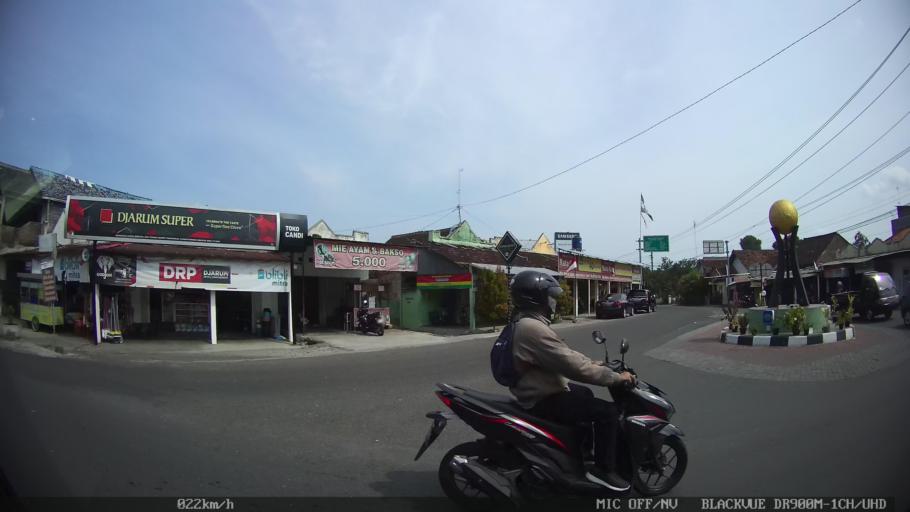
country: ID
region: Daerah Istimewa Yogyakarta
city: Depok
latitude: -7.8047
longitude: 110.4436
